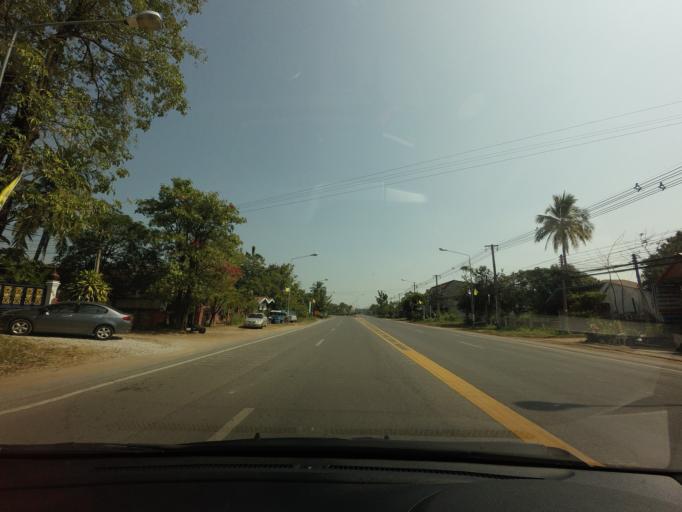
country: TH
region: Sukhothai
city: Ban Na
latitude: 17.0164
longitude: 99.7319
